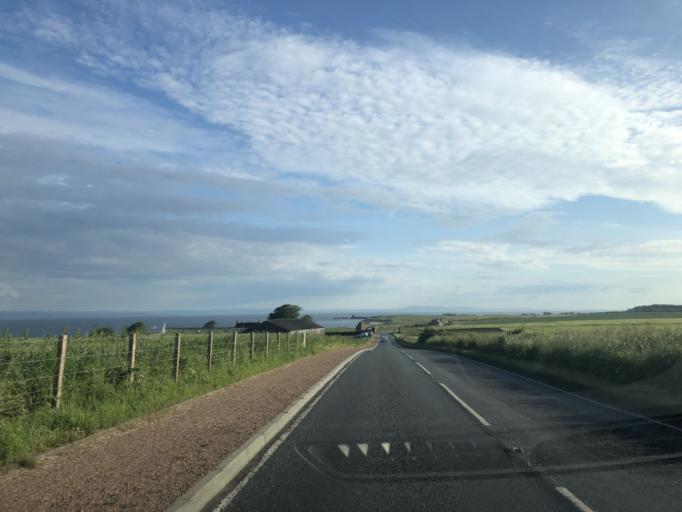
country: GB
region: Scotland
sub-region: Fife
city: Saint Monance
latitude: 56.1991
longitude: -2.7923
